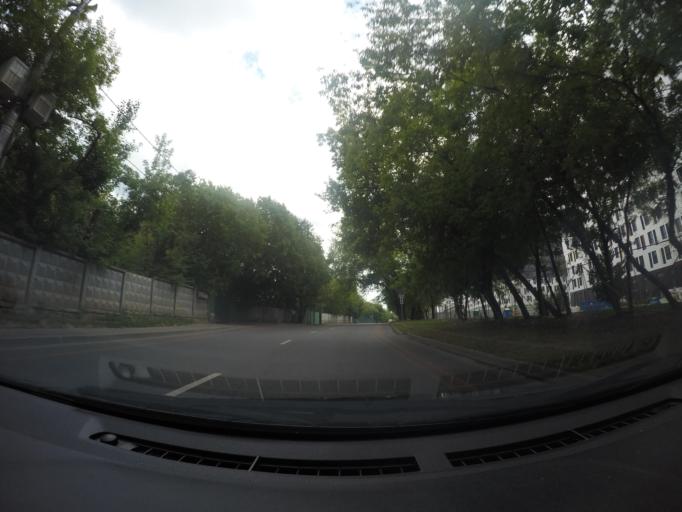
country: RU
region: Moscow
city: Sviblovo
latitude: 55.8558
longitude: 37.6256
